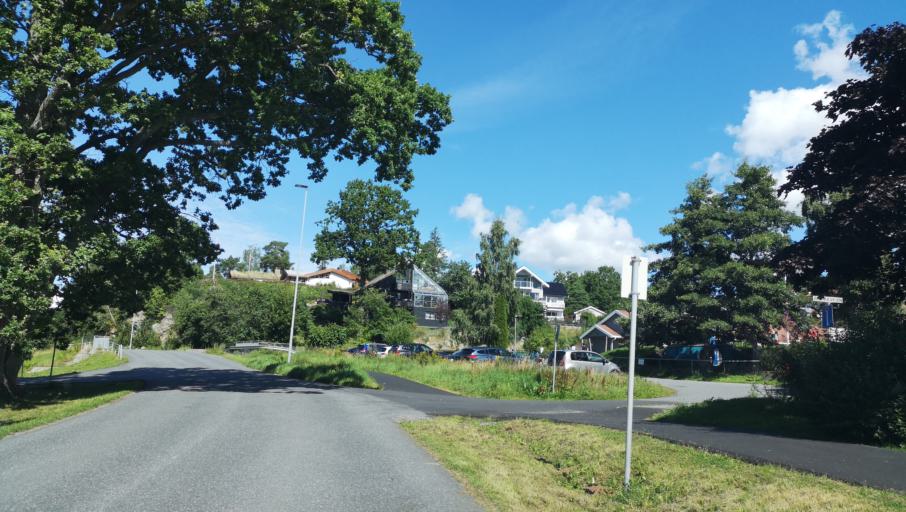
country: NO
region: Akershus
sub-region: Frogn
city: Drobak
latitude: 59.6569
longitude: 10.6419
